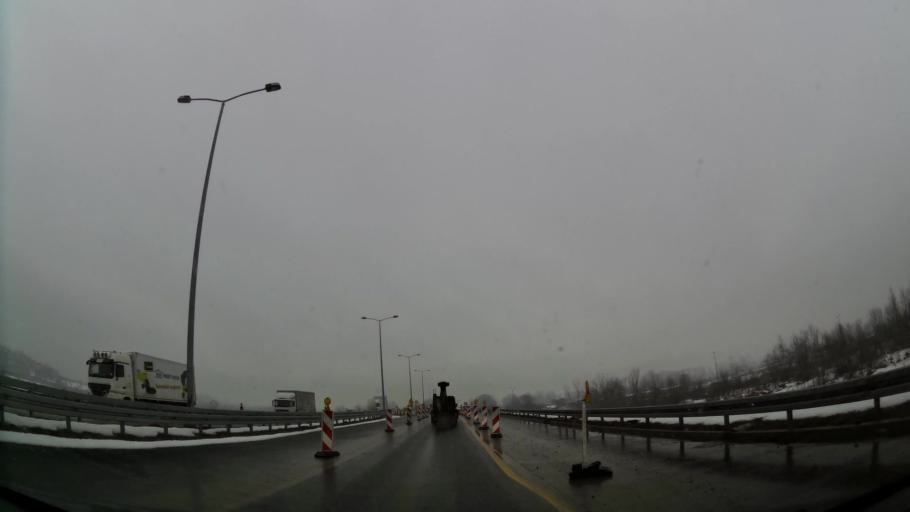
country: RS
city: Ostruznica
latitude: 44.7350
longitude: 20.3316
